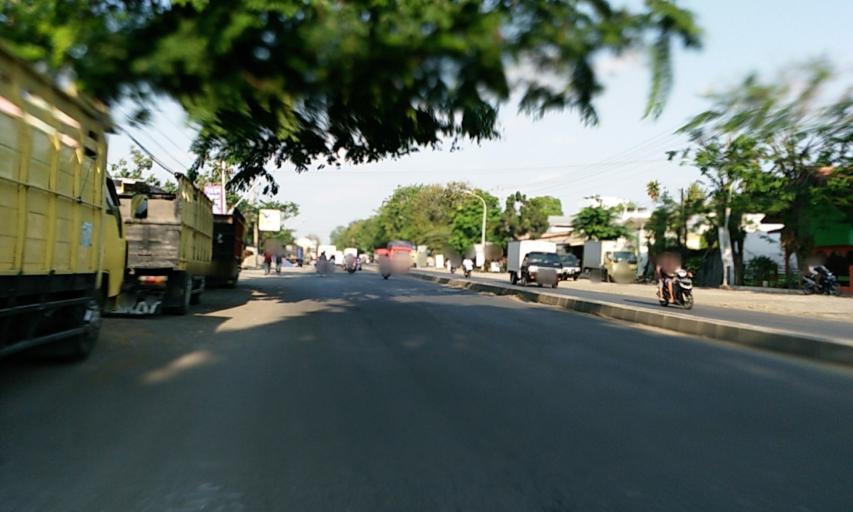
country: ID
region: Central Java
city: Mranggen
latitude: -7.0147
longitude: 110.4820
